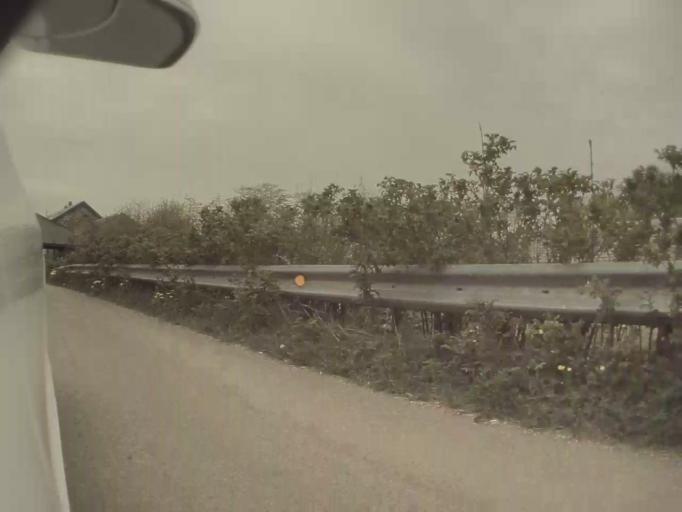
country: BE
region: Wallonia
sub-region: Province du Luxembourg
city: La Roche-en-Ardenne
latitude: 50.2353
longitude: 5.6198
